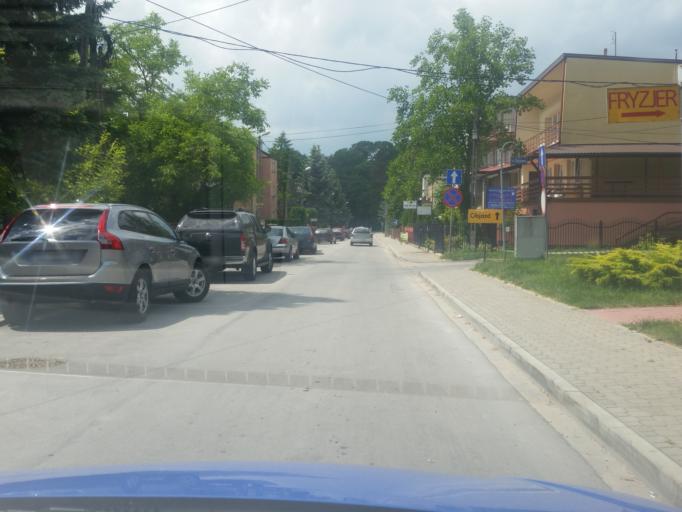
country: PL
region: Swietokrzyskie
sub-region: Powiat buski
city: Busko-Zdroj
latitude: 50.4598
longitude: 20.7254
